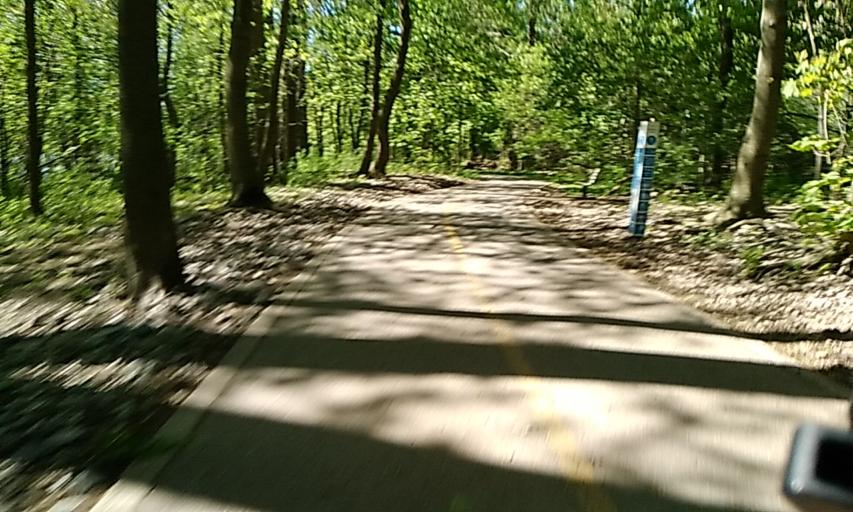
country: CA
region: Ontario
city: London
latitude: 42.9899
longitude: -81.2572
